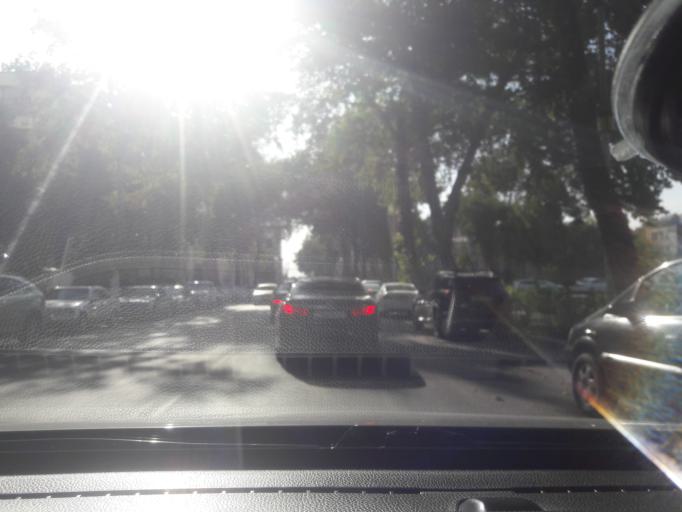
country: TJ
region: Dushanbe
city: Dushanbe
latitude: 38.5812
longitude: 68.7886
